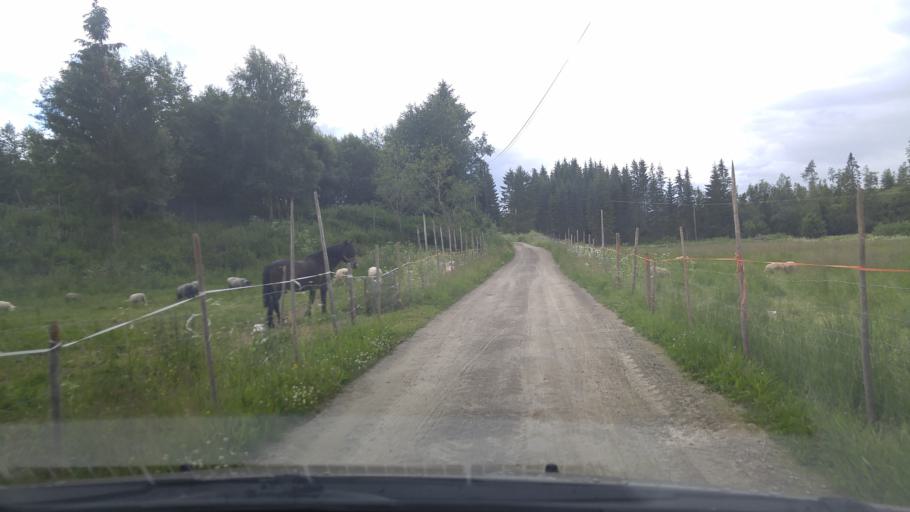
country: NO
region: Nord-Trondelag
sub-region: Levanger
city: Skogn
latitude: 63.6306
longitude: 11.2675
